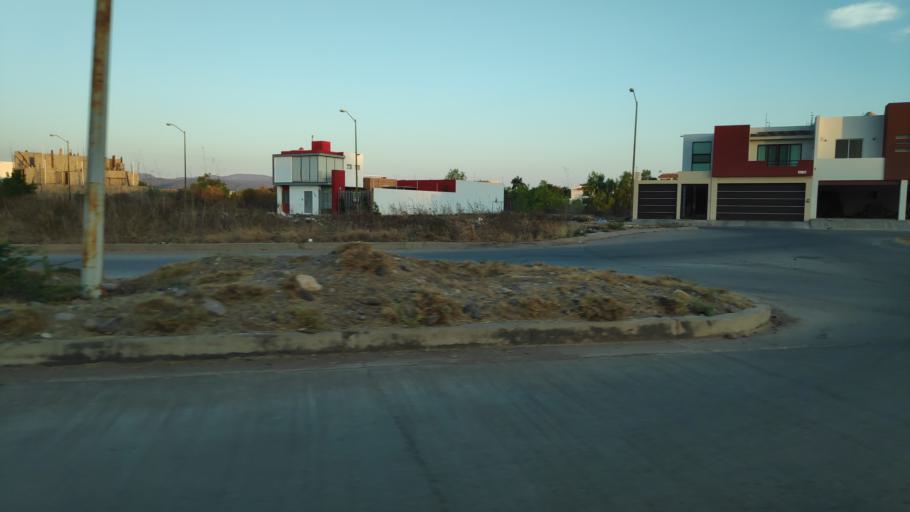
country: MX
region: Sinaloa
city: Culiacan
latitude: 24.8241
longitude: -107.3755
